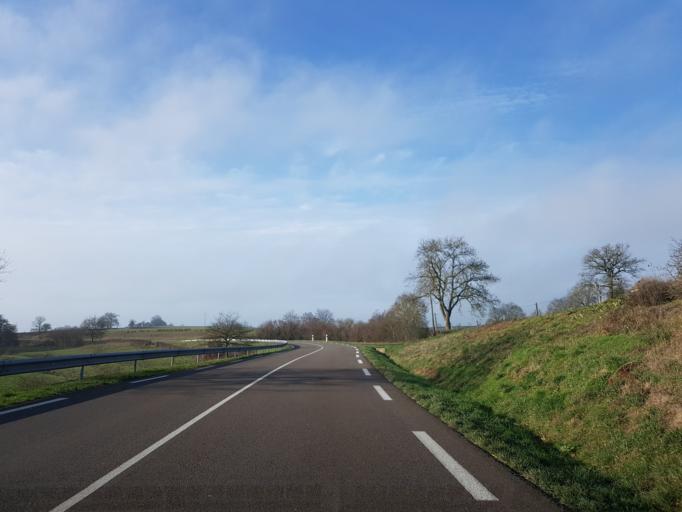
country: FR
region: Bourgogne
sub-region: Departement de Saone-et-Loire
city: Gueugnon
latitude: 46.5992
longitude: 3.9741
